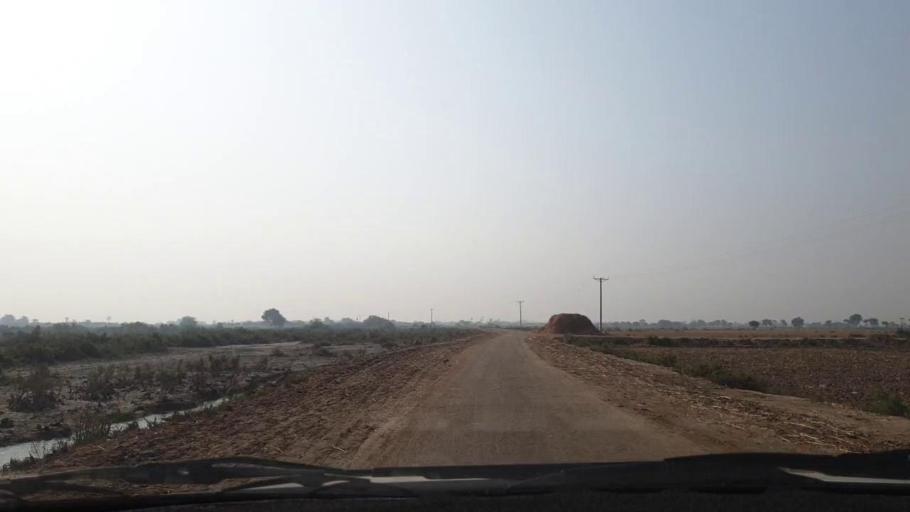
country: PK
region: Sindh
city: Tando Muhammad Khan
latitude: 25.0222
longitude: 68.4500
